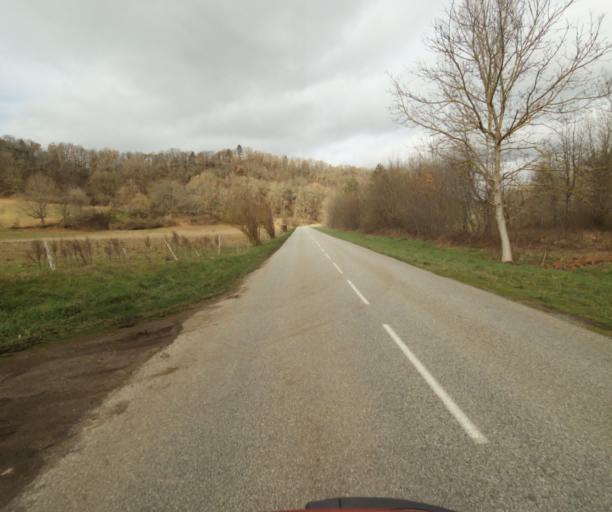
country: FR
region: Midi-Pyrenees
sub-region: Departement de l'Ariege
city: Pamiers
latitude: 43.1444
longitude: 1.5907
